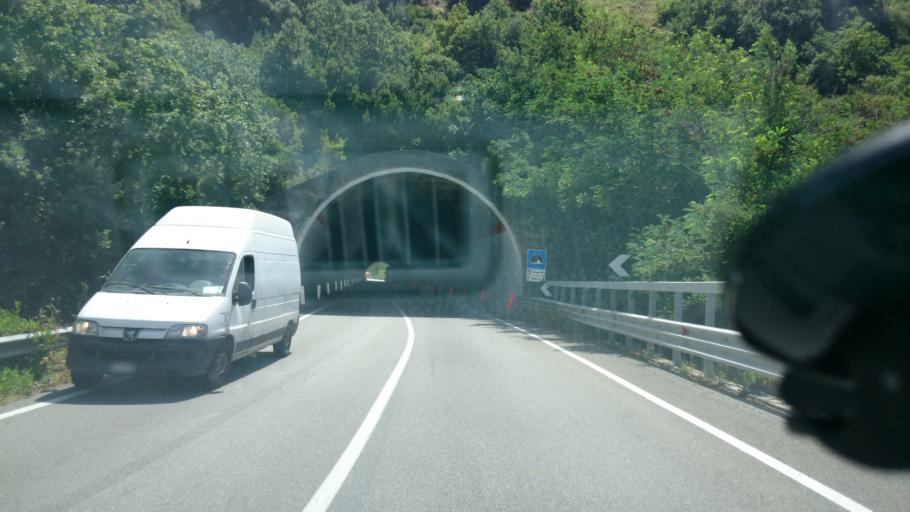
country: IT
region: Calabria
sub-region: Provincia di Cosenza
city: Cittadella del Capo
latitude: 39.5467
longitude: 15.8835
